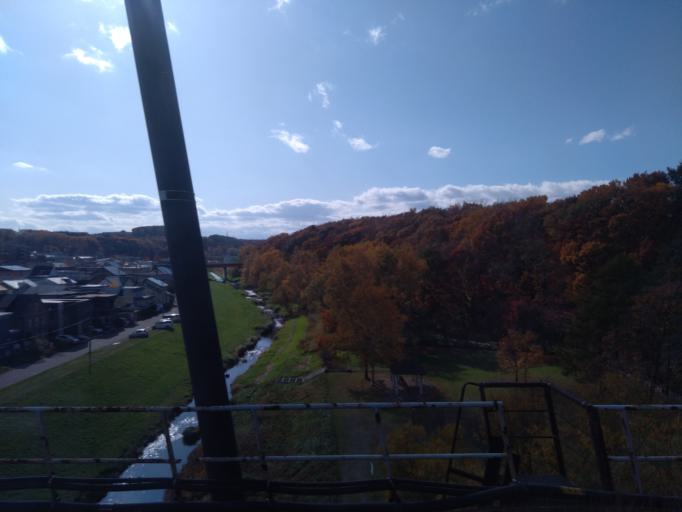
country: JP
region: Hokkaido
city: Kitahiroshima
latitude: 42.9880
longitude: 141.5598
